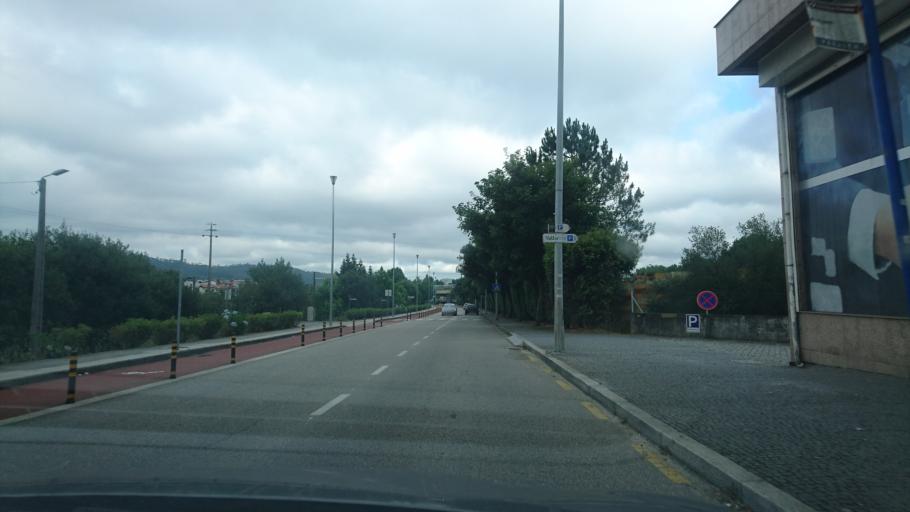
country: PT
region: Porto
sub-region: Valongo
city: Valongo
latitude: 41.1984
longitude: -8.5064
